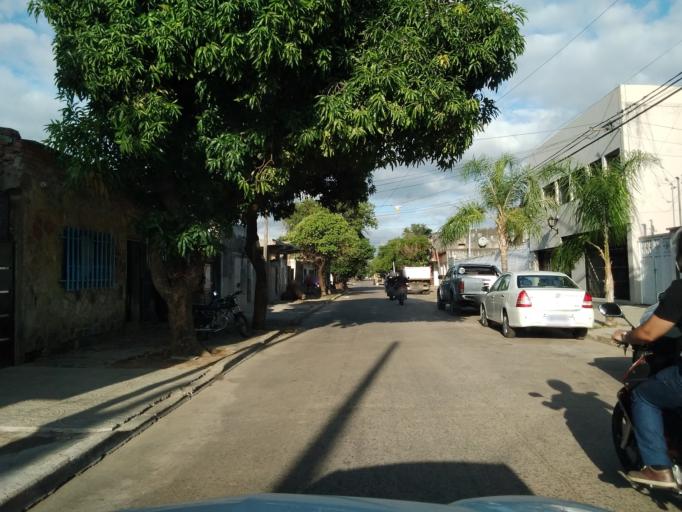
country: AR
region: Corrientes
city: Corrientes
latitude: -27.4656
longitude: -58.8203
